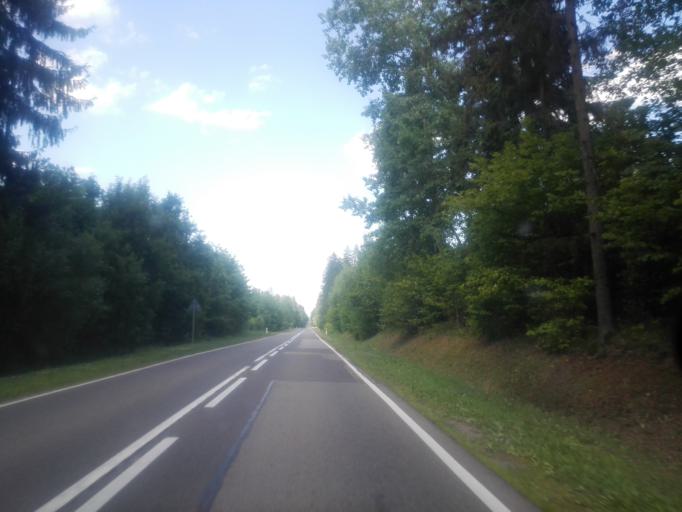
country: PL
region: Podlasie
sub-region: Powiat sejnenski
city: Sejny
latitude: 54.0137
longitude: 23.3327
